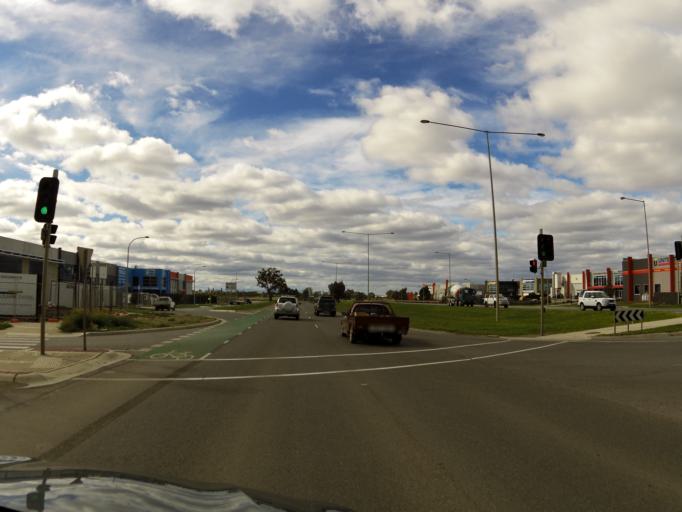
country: AU
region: Victoria
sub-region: Hume
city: Coolaroo
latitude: -37.6455
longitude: 144.9677
